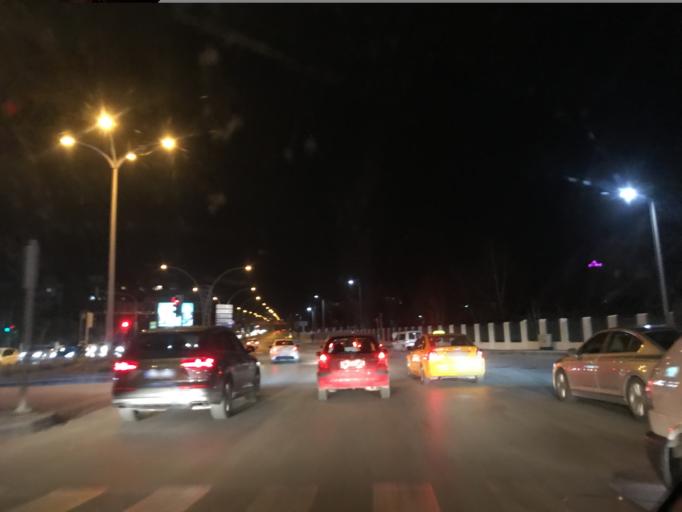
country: TR
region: Ankara
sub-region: Goelbasi
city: Golbasi
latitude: 39.8476
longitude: 32.8406
